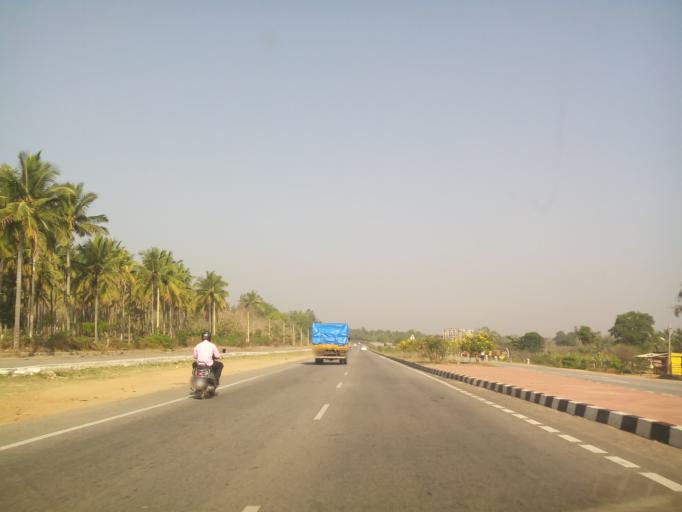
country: IN
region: Karnataka
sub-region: Bangalore Rural
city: Nelamangala
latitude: 13.0638
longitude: 77.3285
